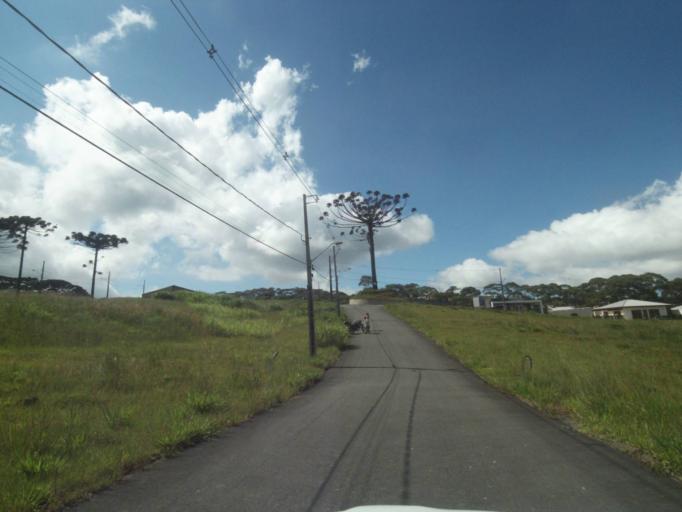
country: BR
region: Parana
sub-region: Colombo
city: Colombo
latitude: -25.3126
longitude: -49.2339
